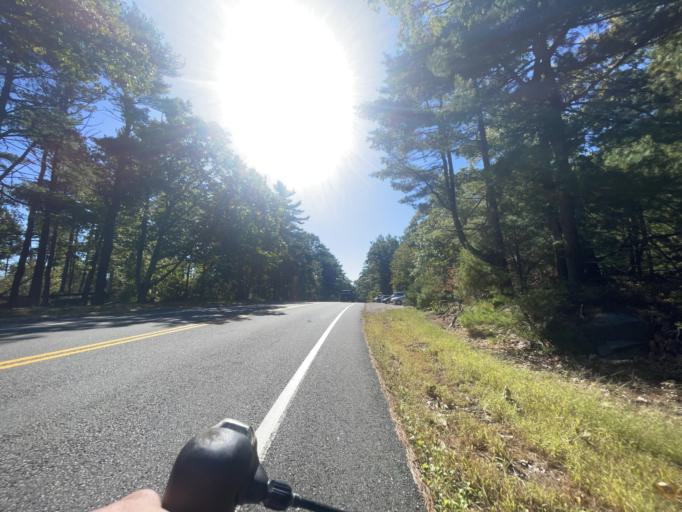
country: US
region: Massachusetts
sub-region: Norfolk County
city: Milton
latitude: 42.2335
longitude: -71.0364
